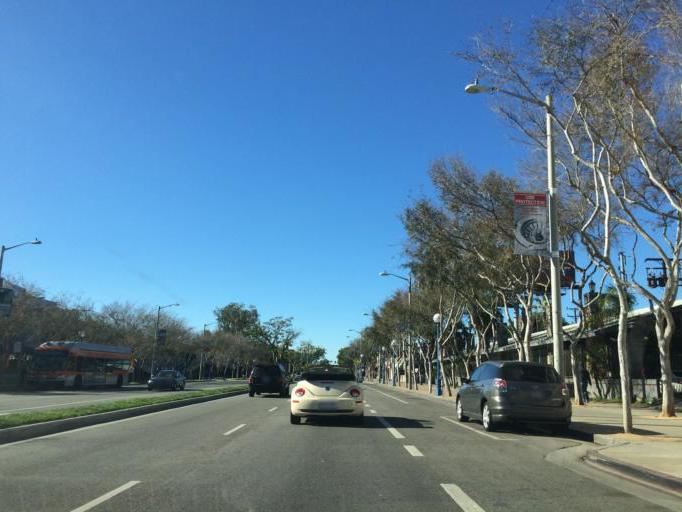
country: US
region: California
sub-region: Los Angeles County
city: West Hollywood
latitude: 34.0866
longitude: -118.3817
